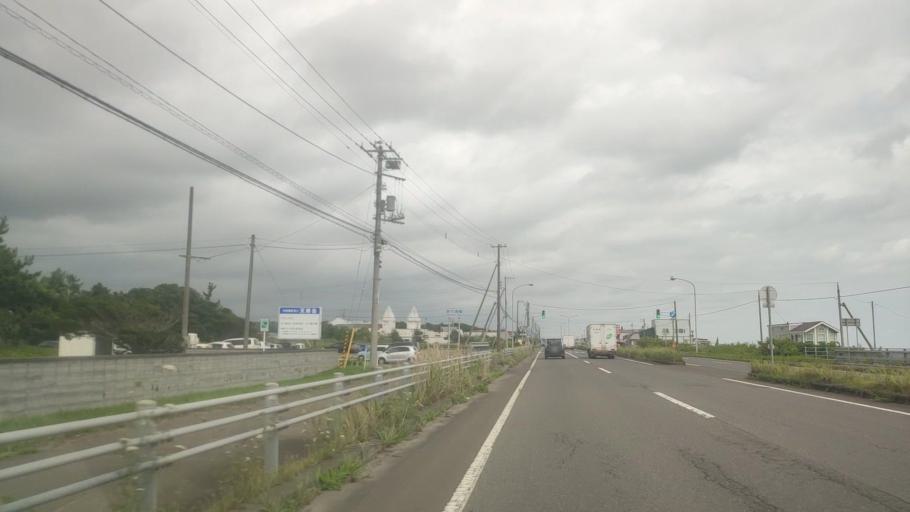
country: JP
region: Hokkaido
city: Shiraoi
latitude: 42.4716
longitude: 141.2321
